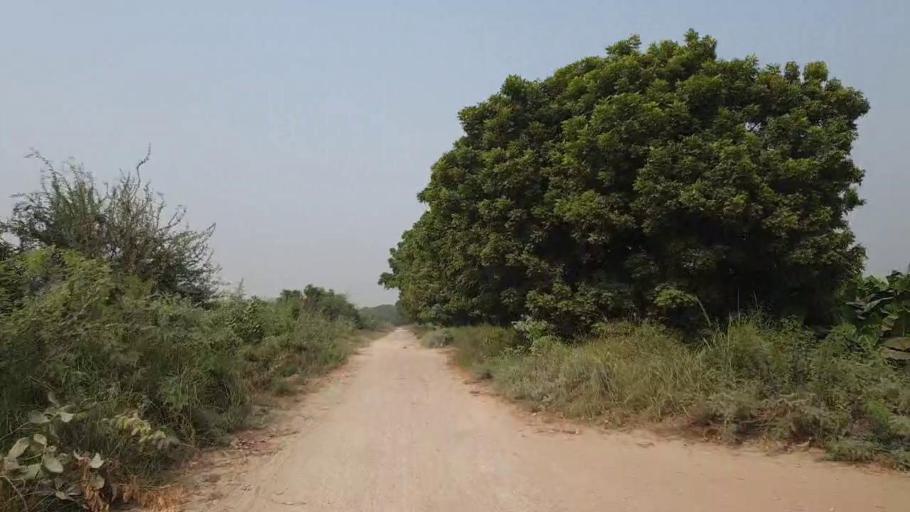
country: PK
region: Sindh
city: Tando Muhammad Khan
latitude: 25.1850
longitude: 68.5968
